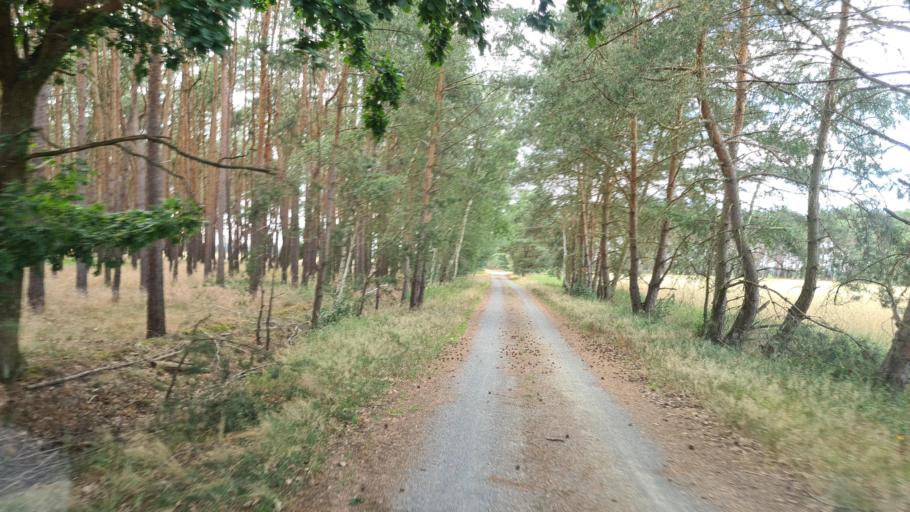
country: DE
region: Saxony-Anhalt
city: Holzdorf
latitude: 51.8149
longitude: 13.1988
